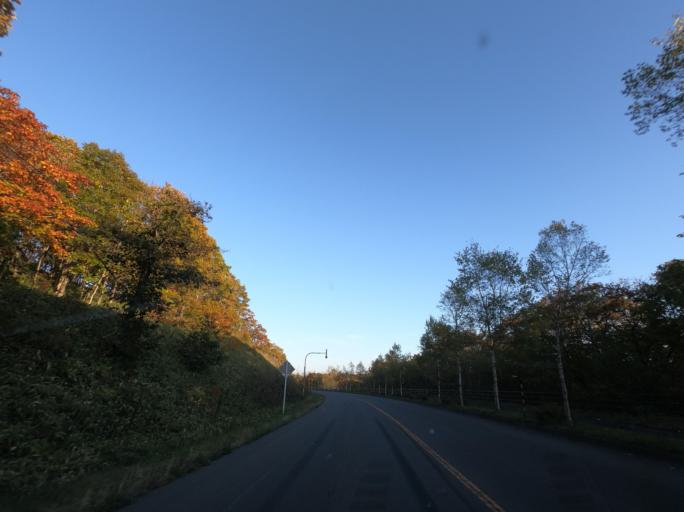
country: JP
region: Hokkaido
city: Kushiro
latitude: 43.0690
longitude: 144.3111
